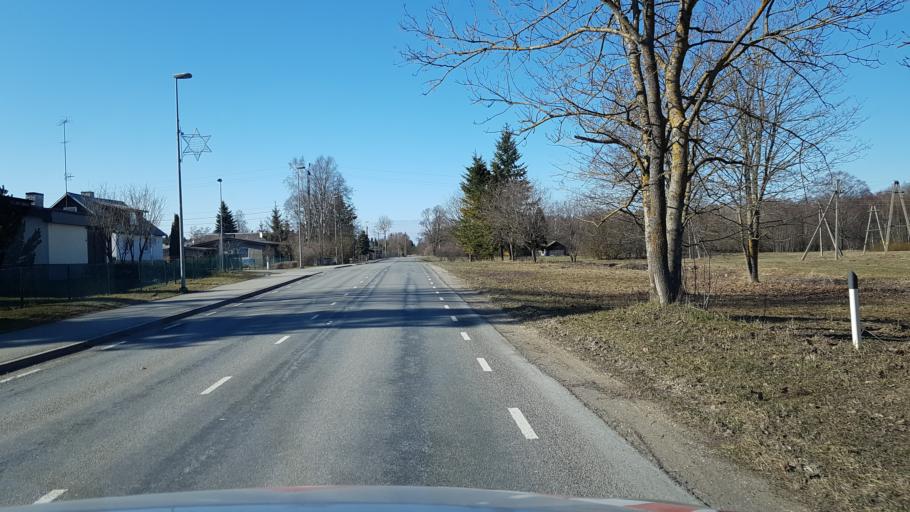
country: EE
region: Laeaene-Virumaa
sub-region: Haljala vald
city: Haljala
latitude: 59.4361
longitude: 26.2649
